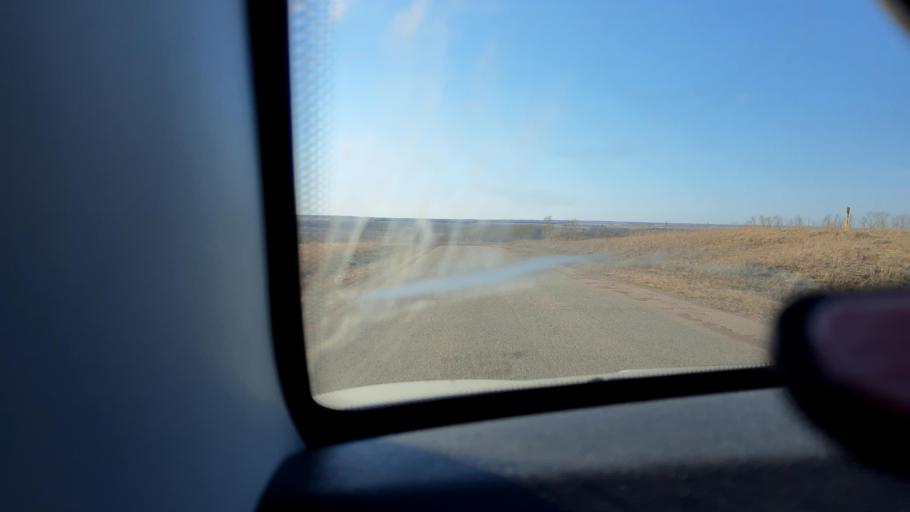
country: RU
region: Bashkortostan
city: Asanovo
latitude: 54.8217
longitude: 55.4718
